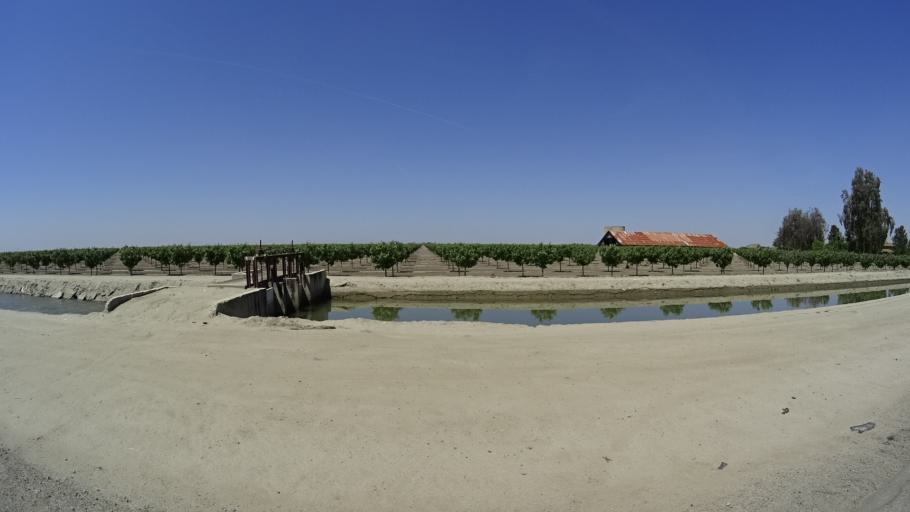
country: US
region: California
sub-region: Kings County
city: Corcoran
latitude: 36.0326
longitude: -119.5360
